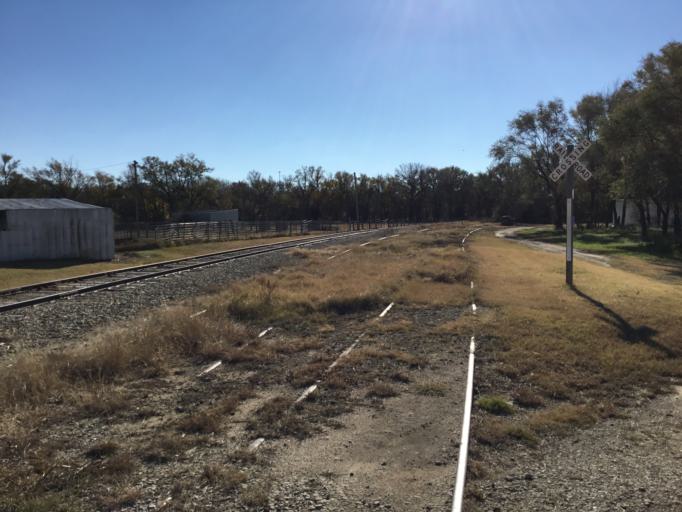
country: US
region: Kansas
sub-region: Lincoln County
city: Lincoln
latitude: 39.0439
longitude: -98.1555
